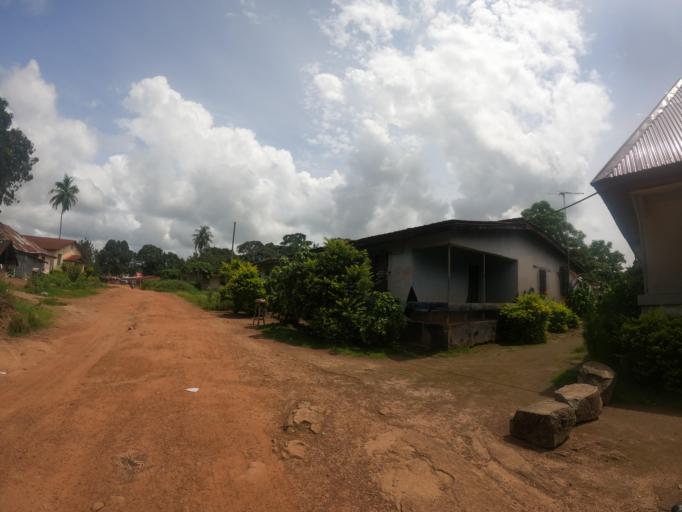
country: SL
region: Northern Province
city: Makeni
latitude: 8.8957
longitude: -12.0571
